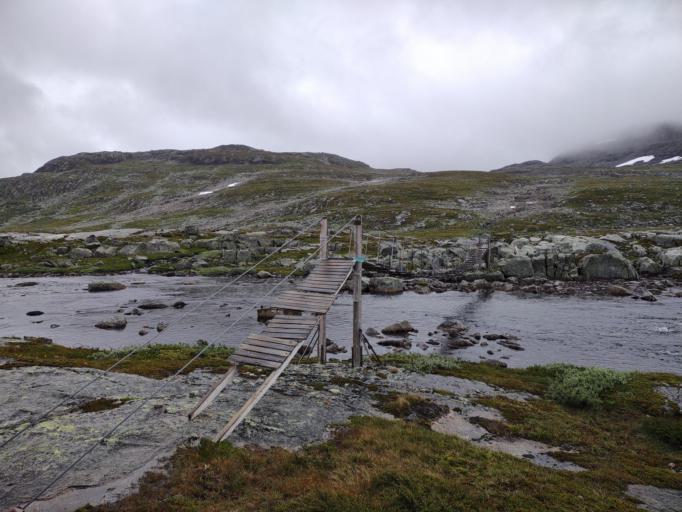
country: NO
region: Aust-Agder
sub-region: Bykle
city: Hovden
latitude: 59.9799
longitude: 7.2240
